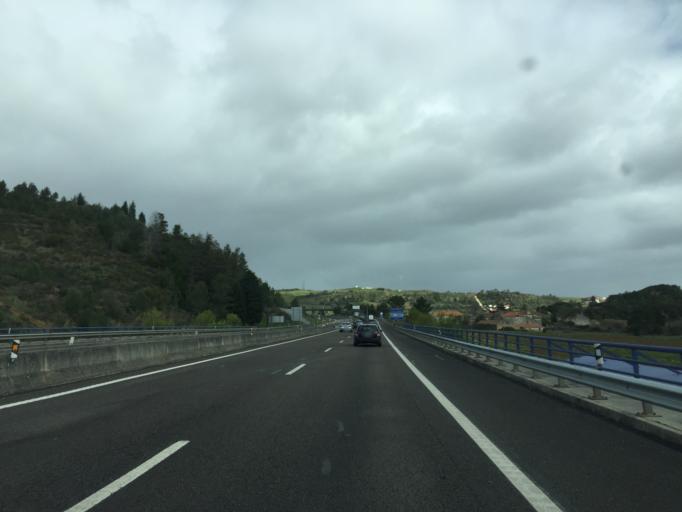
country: PT
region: Lisbon
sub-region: Torres Vedras
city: Torres Vedras
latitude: 39.0823
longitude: -9.2319
